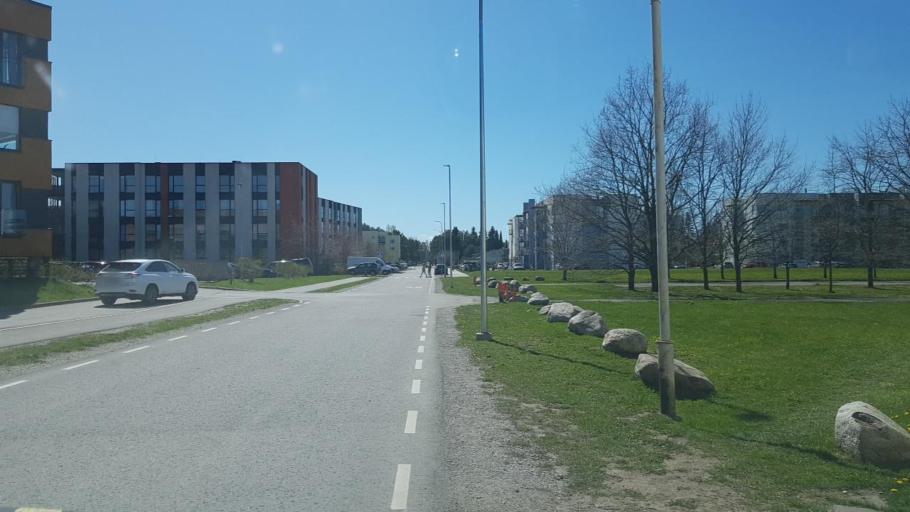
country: EE
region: Harju
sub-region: Viimsi vald
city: Haabneeme
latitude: 59.5148
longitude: 24.8273
